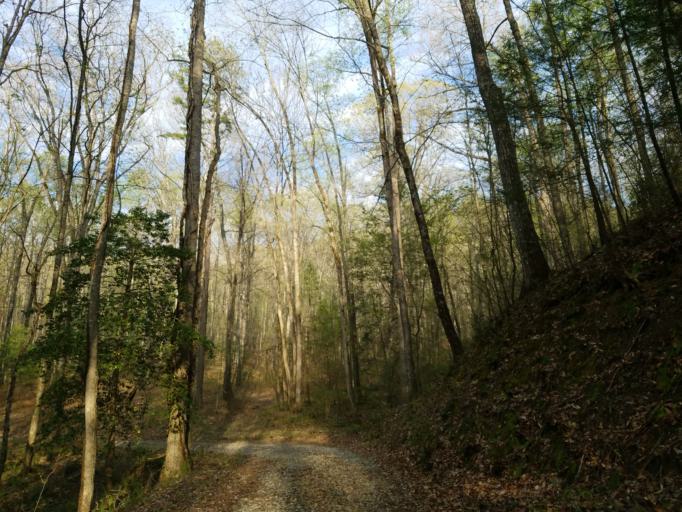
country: US
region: Georgia
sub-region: Fannin County
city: Blue Ridge
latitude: 34.7225
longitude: -84.1983
